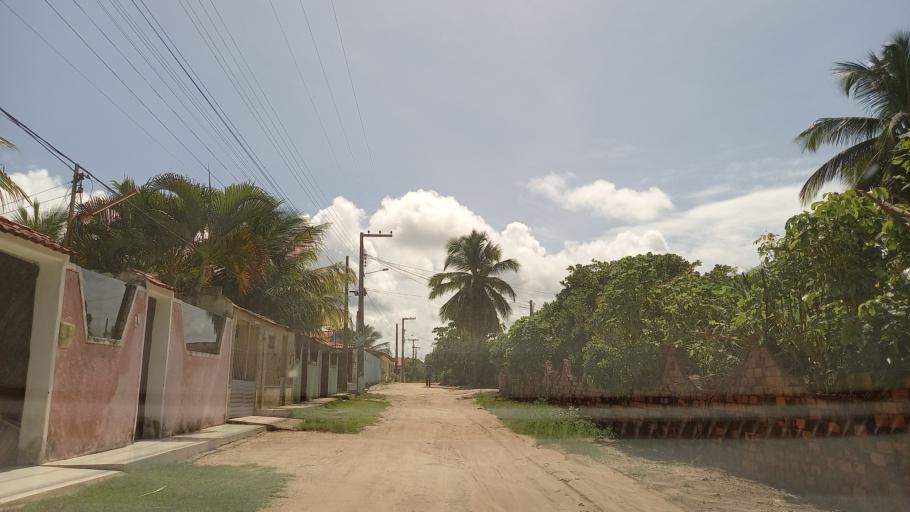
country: BR
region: Pernambuco
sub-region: Sao Jose Da Coroa Grande
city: Sao Jose da Coroa Grande
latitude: -8.9222
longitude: -35.1645
